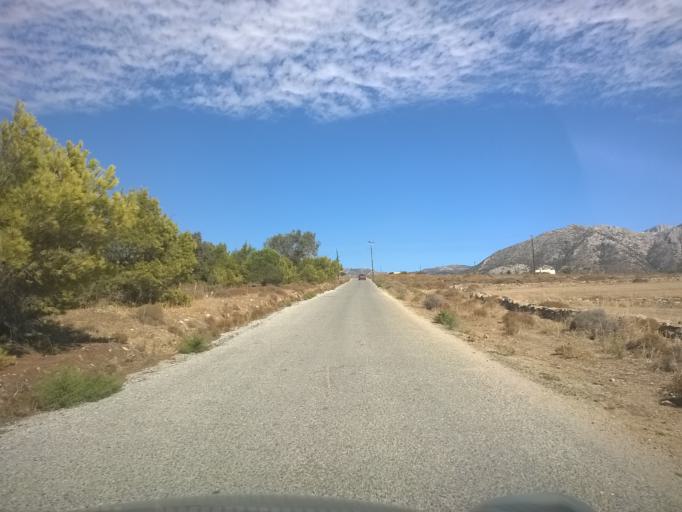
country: GR
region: South Aegean
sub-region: Nomos Kykladon
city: Filotion
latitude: 37.0371
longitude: 25.4287
